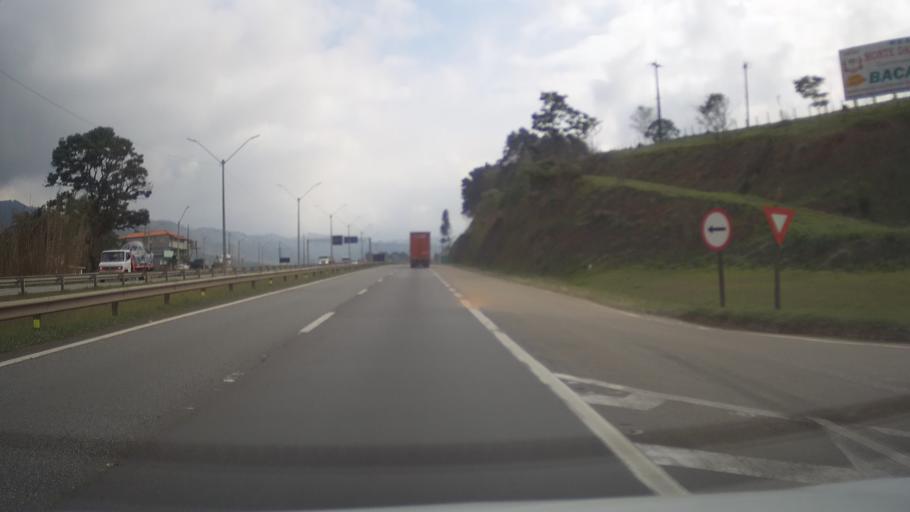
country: BR
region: Minas Gerais
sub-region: Extrema
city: Extrema
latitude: -22.9031
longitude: -46.4213
